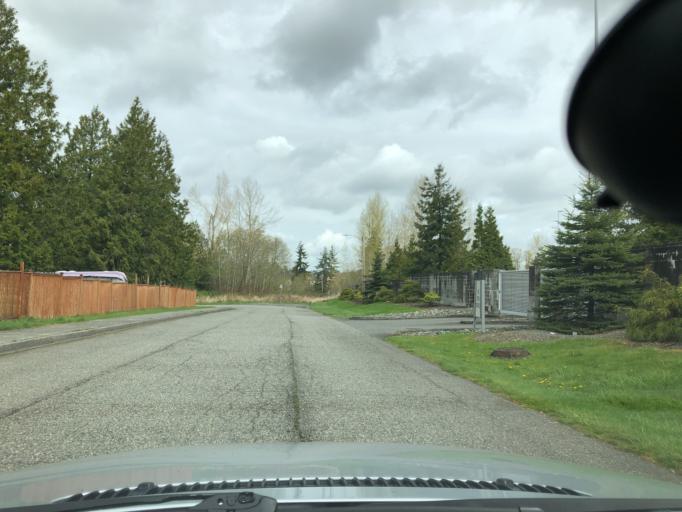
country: US
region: Washington
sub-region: Whatcom County
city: Blaine
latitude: 49.0005
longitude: -122.7401
